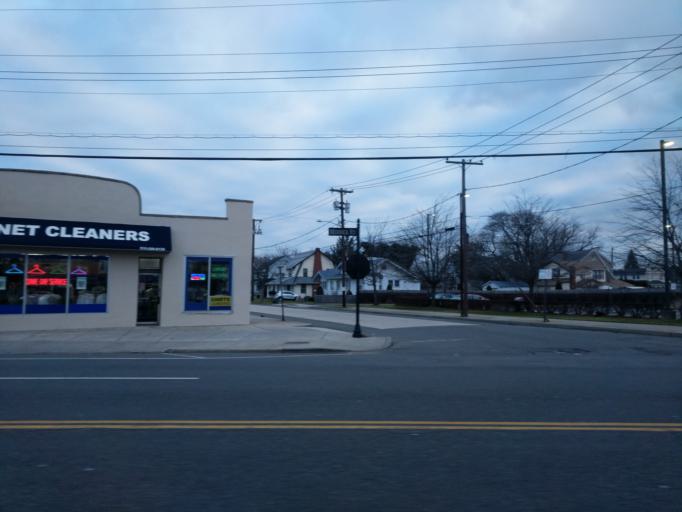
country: US
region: New York
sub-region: Nassau County
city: Lynbrook
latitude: 40.6602
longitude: -73.6828
